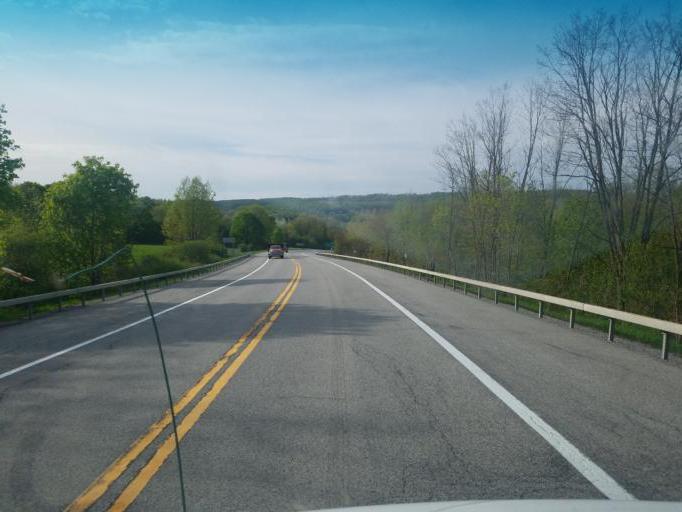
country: US
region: New York
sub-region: Herkimer County
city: Little Falls
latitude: 43.0230
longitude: -74.8193
